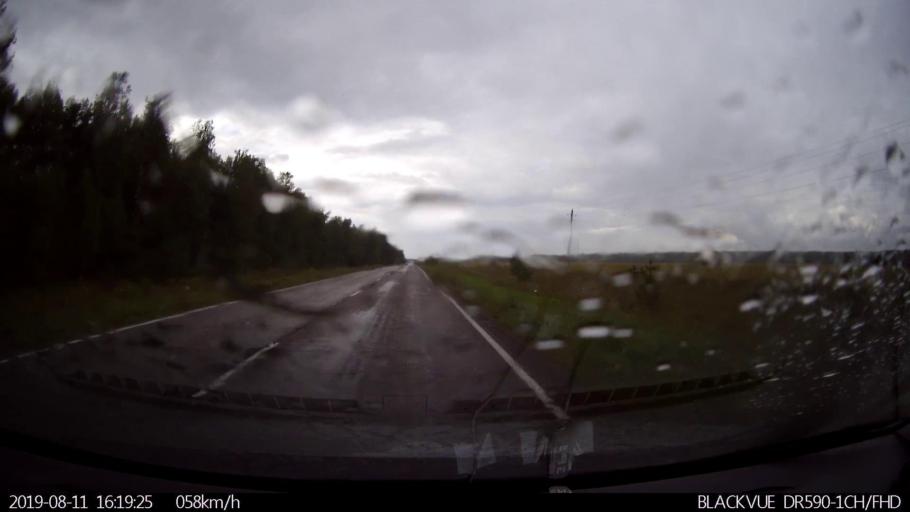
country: RU
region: Ulyanovsk
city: Mayna
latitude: 54.0634
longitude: 47.6075
